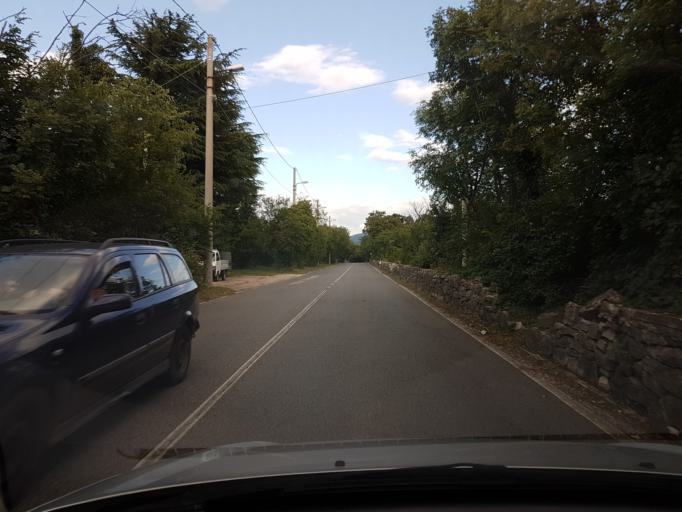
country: IT
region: Friuli Venezia Giulia
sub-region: Provincia di Trieste
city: Villa Opicina
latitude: 45.6793
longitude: 13.8080
